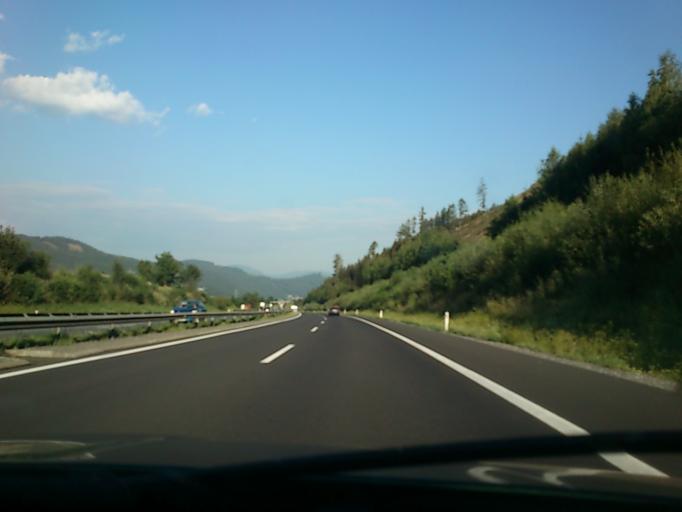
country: AT
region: Styria
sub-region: Politischer Bezirk Leoben
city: Kammern im Liesingtal
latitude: 47.3846
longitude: 14.9228
